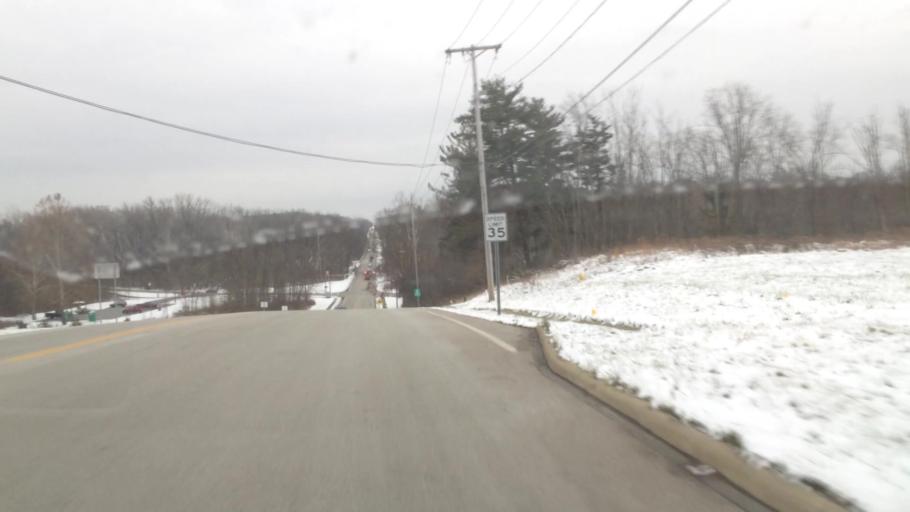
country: US
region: Ohio
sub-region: Cuyahoga County
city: Strongsville
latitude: 41.3130
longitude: -81.7854
